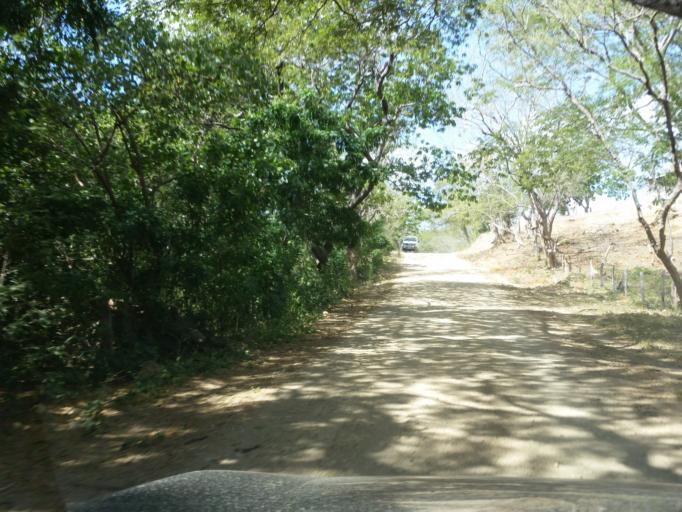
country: CR
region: Guanacaste
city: La Cruz
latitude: 11.1108
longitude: -85.7550
